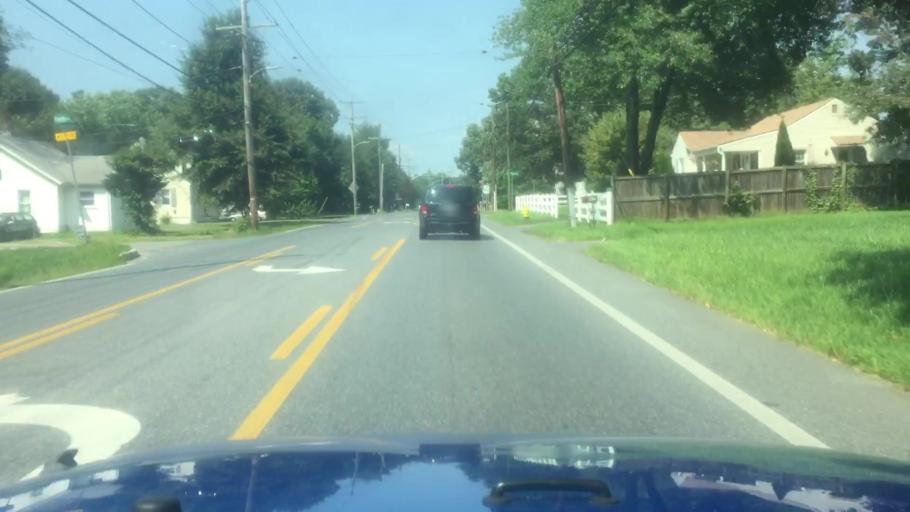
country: US
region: Maryland
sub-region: Anne Arundel County
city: Severn
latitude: 39.1177
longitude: -76.6910
